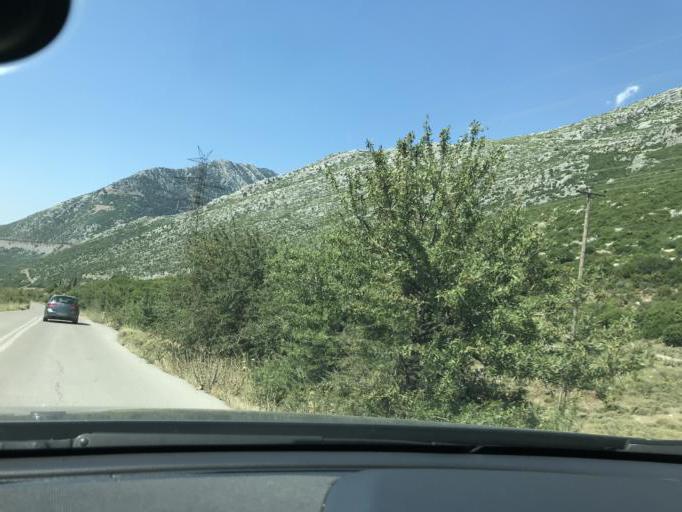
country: GR
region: Central Greece
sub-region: Nomos Voiotias
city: Distomo
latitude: 38.4903
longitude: 22.6926
